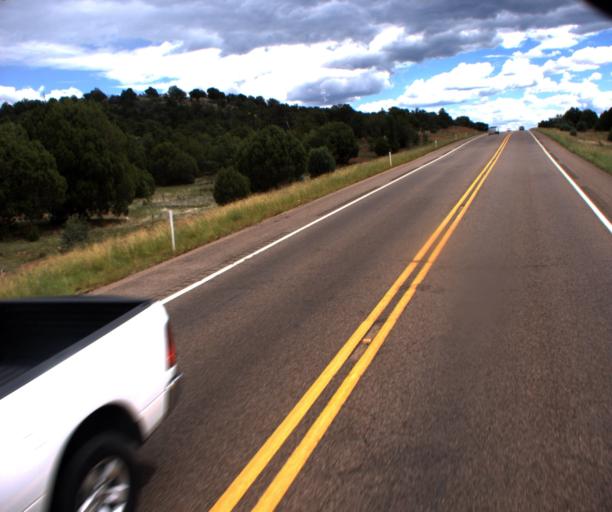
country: US
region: Arizona
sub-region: Navajo County
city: Linden
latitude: 34.2979
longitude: -110.1921
